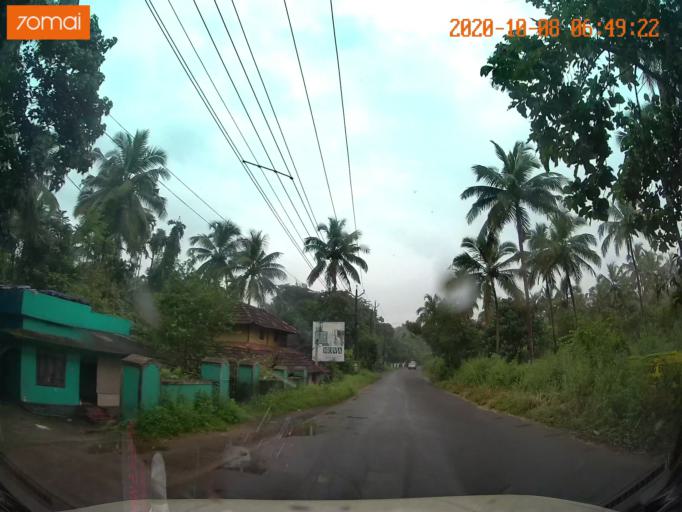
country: IN
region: Kerala
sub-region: Thrissur District
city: Kunnamkulam
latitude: 10.6828
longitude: 76.1028
